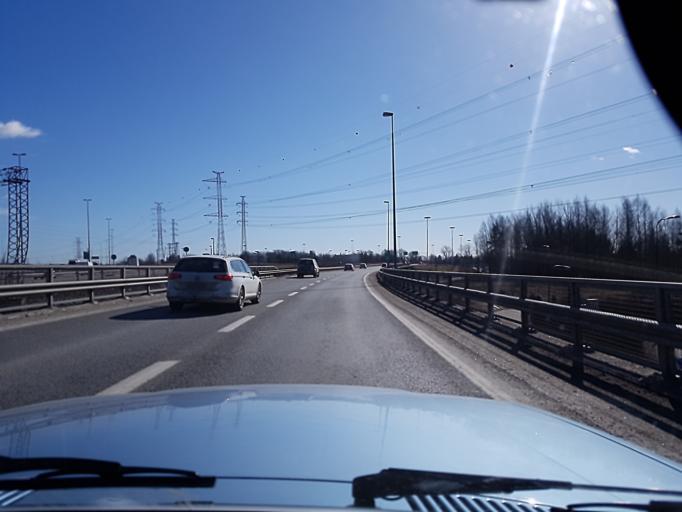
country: FI
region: Uusimaa
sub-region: Helsinki
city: Vantaa
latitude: 60.2892
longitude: 24.9749
